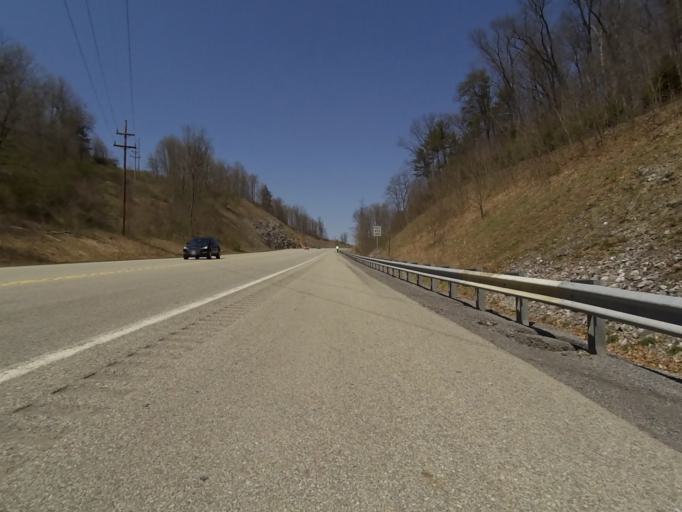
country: US
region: Pennsylvania
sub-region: Blair County
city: Williamsburg
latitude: 40.5730
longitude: -78.1396
